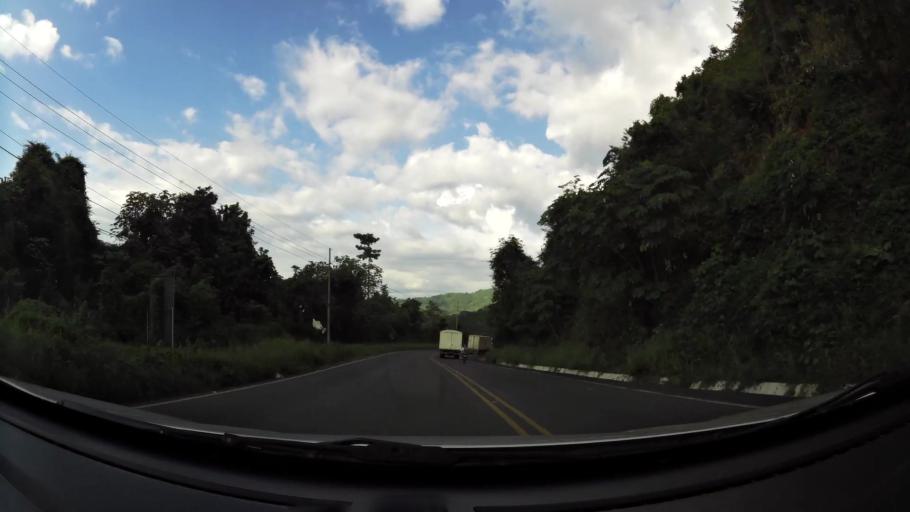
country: CR
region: Puntarenas
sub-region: Canton de Garabito
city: Jaco
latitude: 9.7016
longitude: -84.6382
